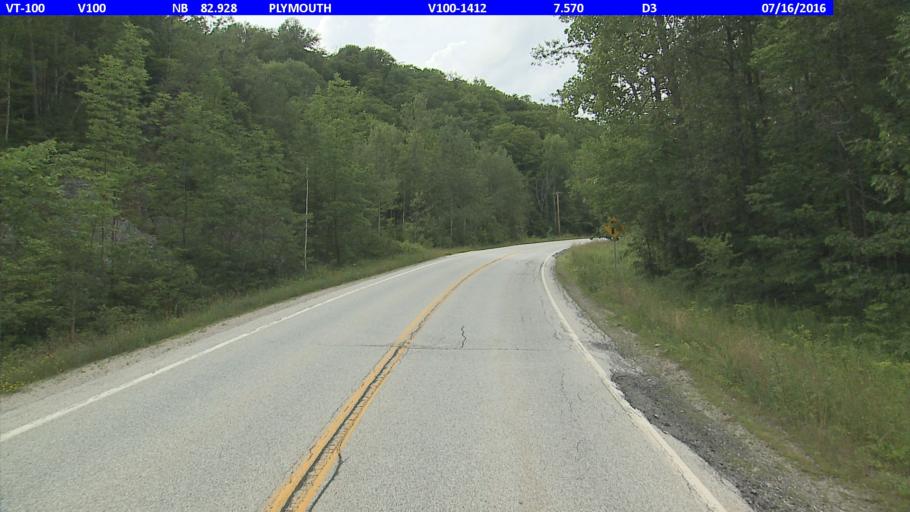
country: US
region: Vermont
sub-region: Rutland County
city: Rutland
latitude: 43.5579
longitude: -72.7594
